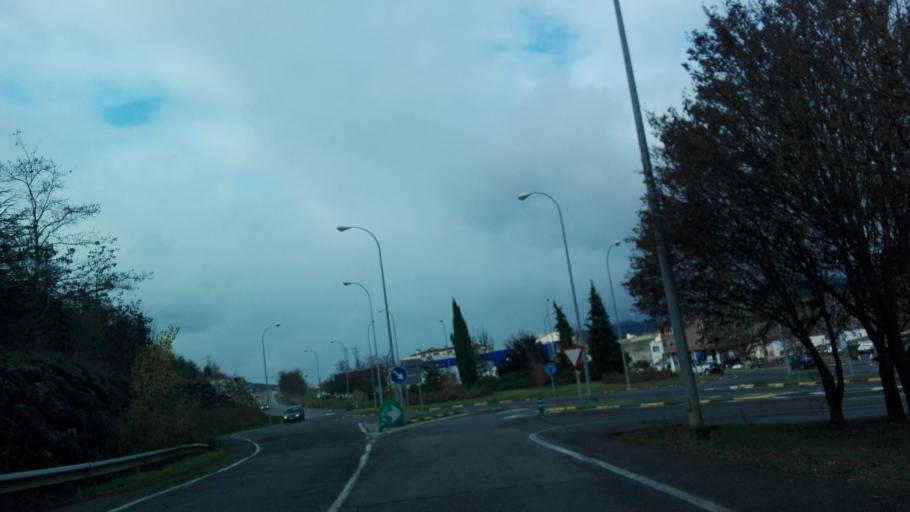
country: ES
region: Navarre
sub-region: Provincia de Navarra
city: Atarrabia
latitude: 42.8385
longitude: -1.6078
